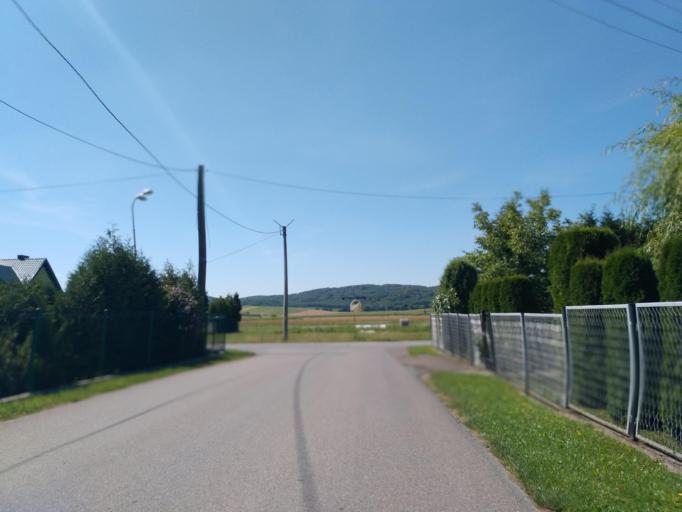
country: PL
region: Subcarpathian Voivodeship
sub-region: Powiat sanocki
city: Dlugie
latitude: 49.5742
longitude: 22.0402
